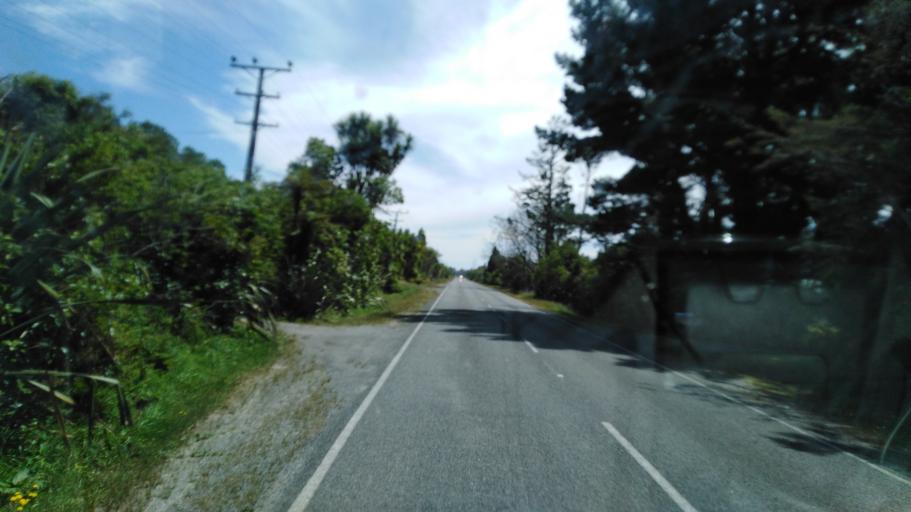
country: NZ
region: West Coast
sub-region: Buller District
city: Westport
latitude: -41.7448
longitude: 171.7174
